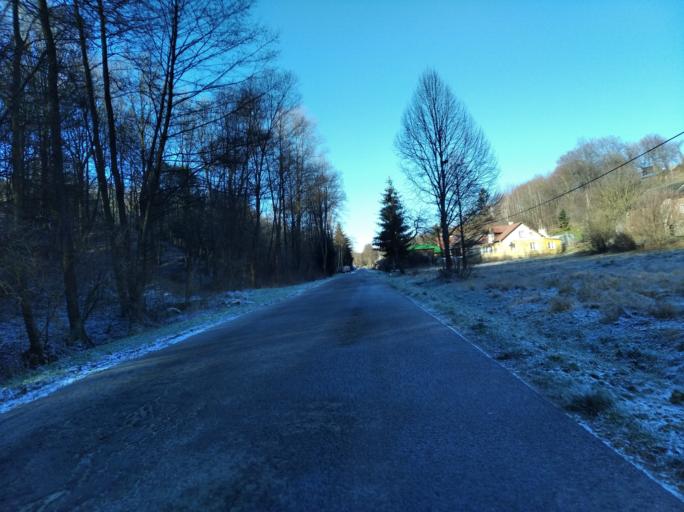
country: PL
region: Subcarpathian Voivodeship
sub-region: Powiat strzyzowski
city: Czudec
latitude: 49.9476
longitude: 21.7831
